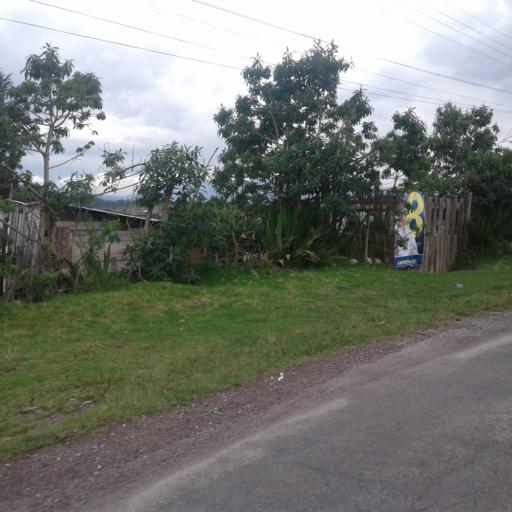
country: EC
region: Pichincha
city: Sangolqui
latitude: -0.2925
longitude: -78.3873
